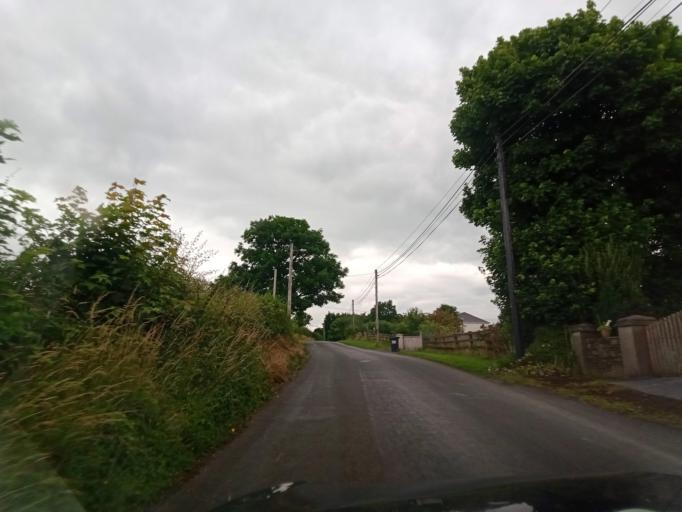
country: IE
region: Leinster
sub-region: Kilkenny
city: Castlecomer
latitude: 52.8923
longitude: -7.1543
